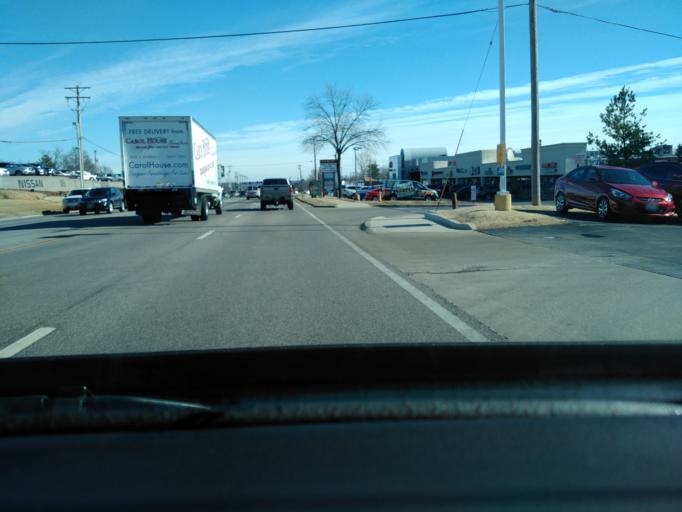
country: US
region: Missouri
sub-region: Saint Louis County
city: Winchester
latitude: 38.5929
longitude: -90.5336
